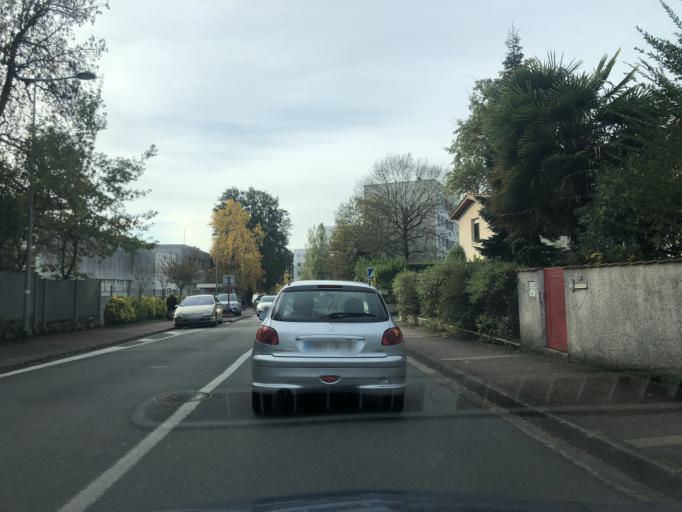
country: FR
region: Aquitaine
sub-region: Departement de la Gironde
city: Merignac
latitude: 44.8435
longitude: -0.6503
